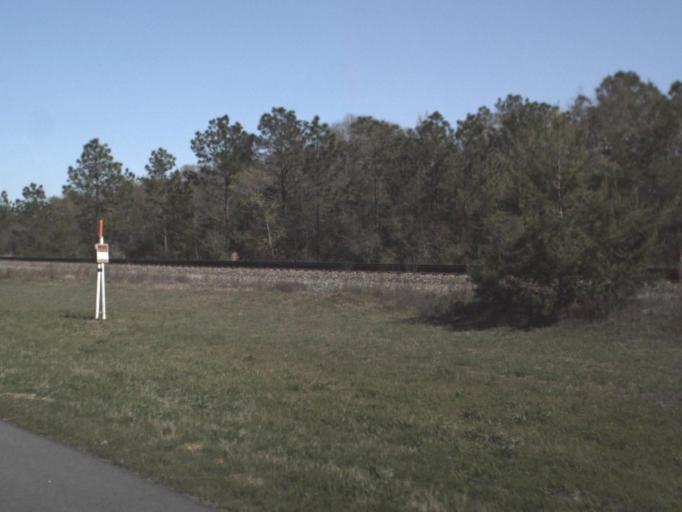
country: US
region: Florida
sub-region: Walton County
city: DeFuniak Springs
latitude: 30.7512
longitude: -86.2852
